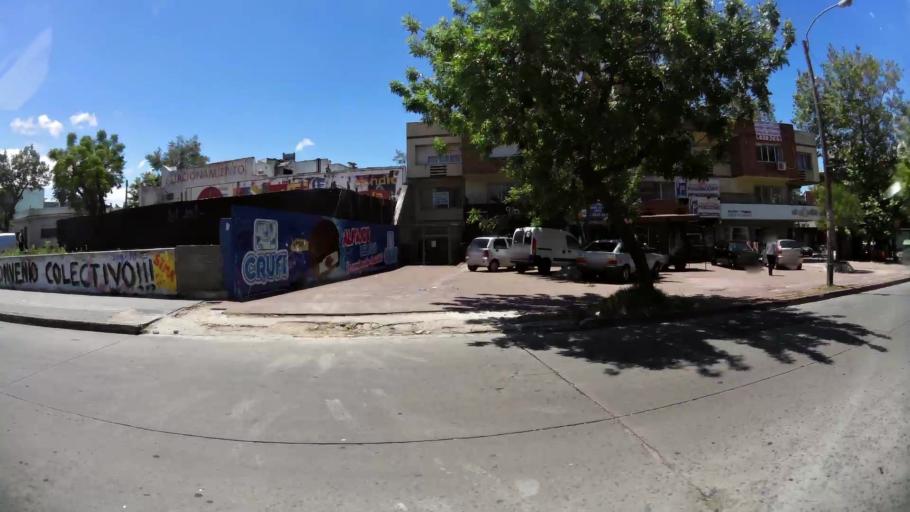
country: UY
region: Montevideo
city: Montevideo
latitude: -34.9009
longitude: -56.1386
